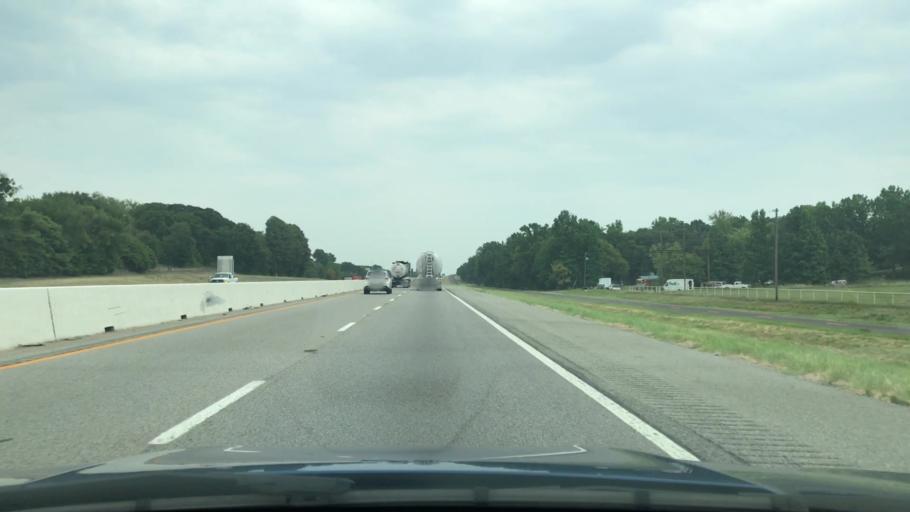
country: US
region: Texas
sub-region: Van Zandt County
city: Canton
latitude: 32.5538
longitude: -95.7900
